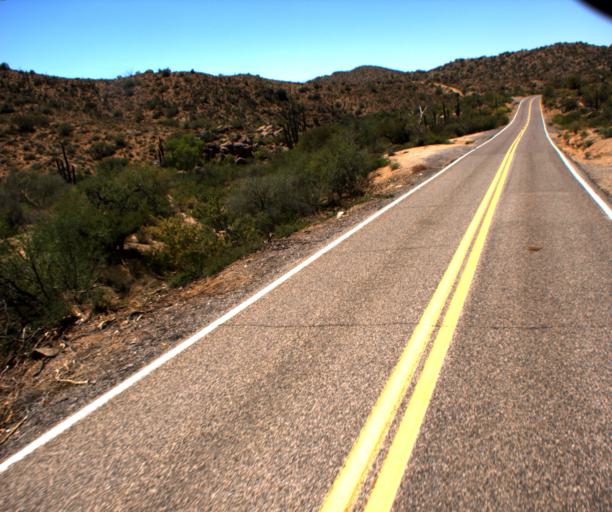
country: US
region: Arizona
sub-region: Yavapai County
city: Bagdad
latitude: 34.4537
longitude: -112.9913
